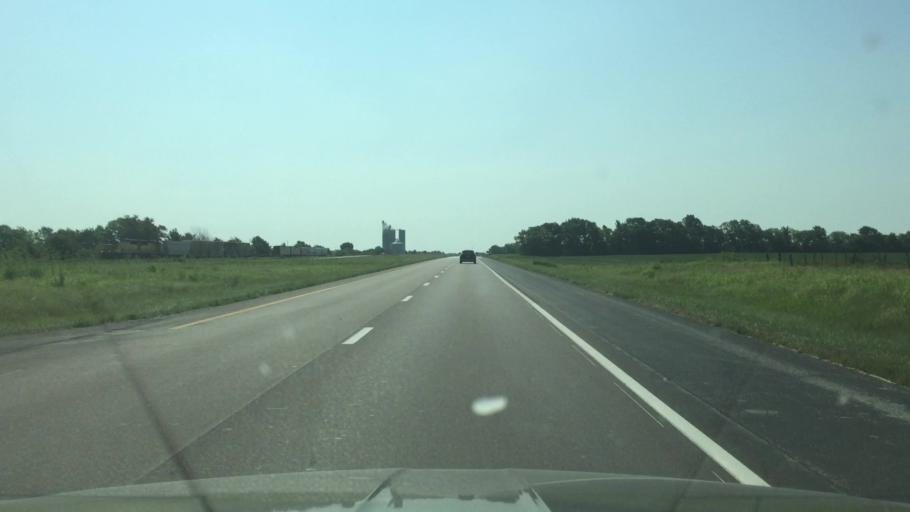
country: US
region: Missouri
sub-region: Pettis County
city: La Monte
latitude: 38.7563
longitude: -93.3638
